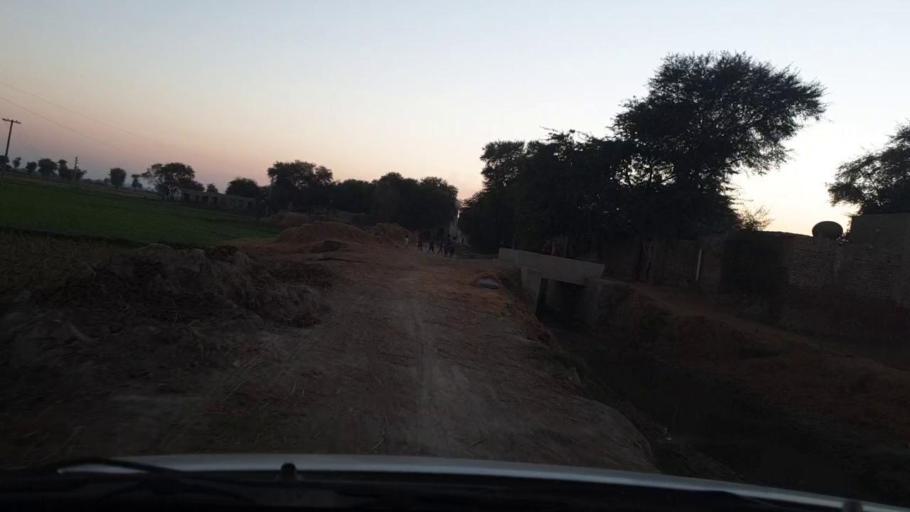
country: PK
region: Sindh
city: Khairpur Nathan Shah
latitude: 27.1472
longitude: 67.6886
